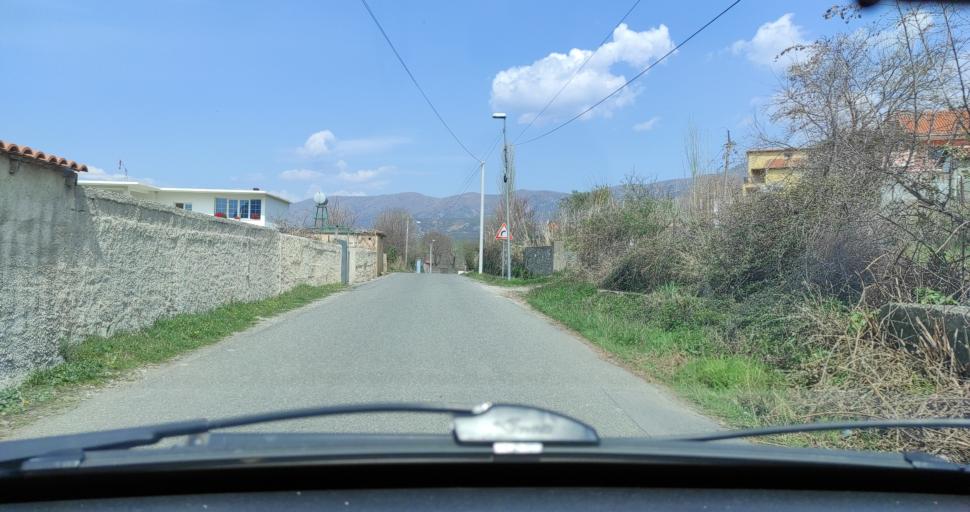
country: AL
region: Lezhe
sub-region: Rrethi i Lezhes
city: Kallmeti i Madh
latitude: 41.8550
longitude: 19.6950
